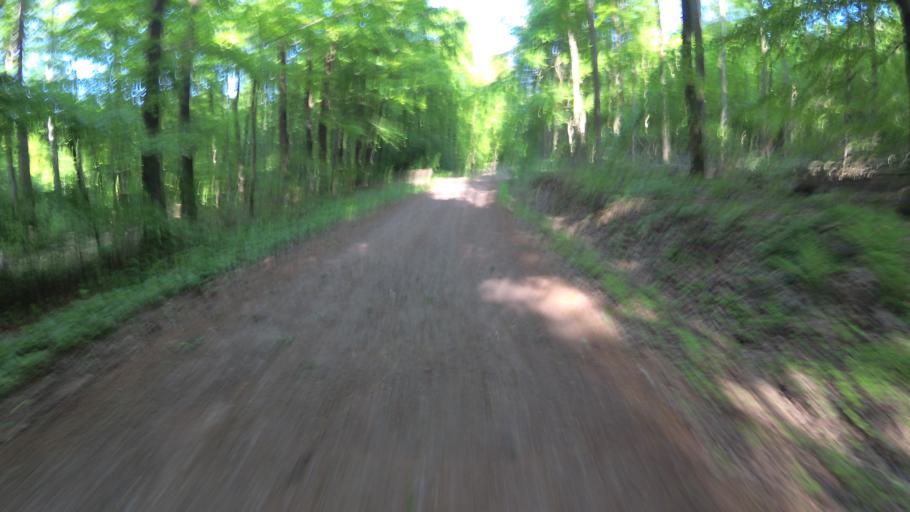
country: DE
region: Saarland
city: Marpingen
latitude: 49.4226
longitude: 7.0521
